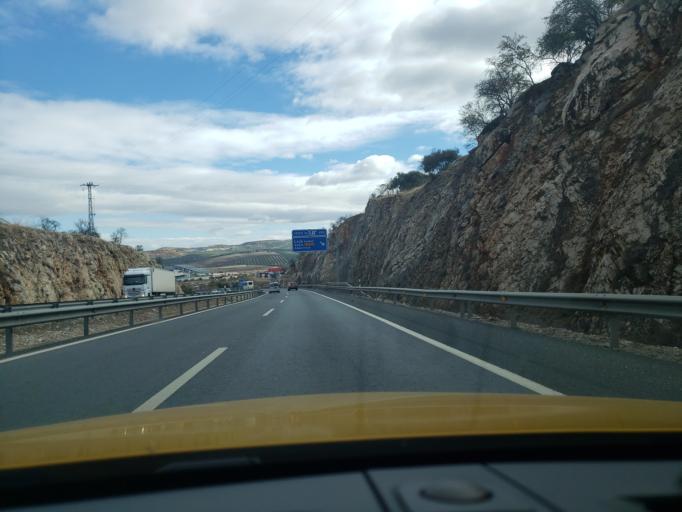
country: ES
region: Andalusia
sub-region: Provincia de Granada
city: Loja
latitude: 37.1599
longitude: -4.1361
